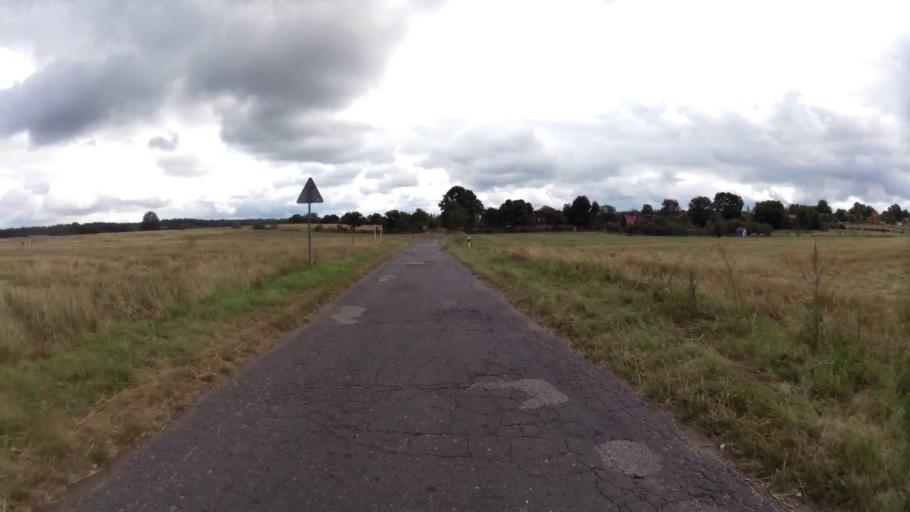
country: PL
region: West Pomeranian Voivodeship
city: Trzcinsko Zdroj
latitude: 52.8881
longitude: 14.7133
